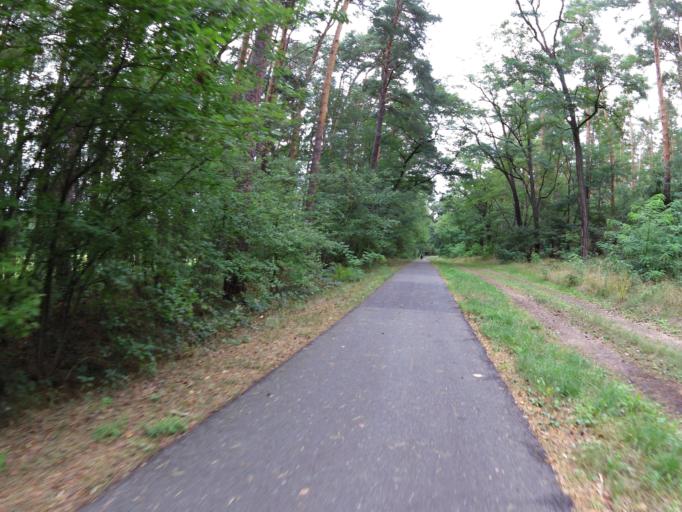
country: DE
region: Brandenburg
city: Reichenwalde
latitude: 52.2477
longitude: 13.9788
